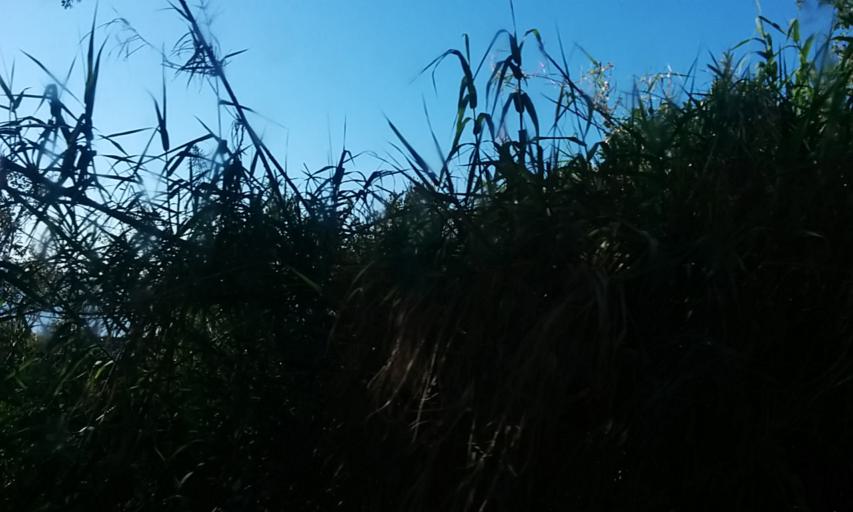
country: JP
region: Wakayama
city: Minato
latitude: 34.1902
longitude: 135.1481
